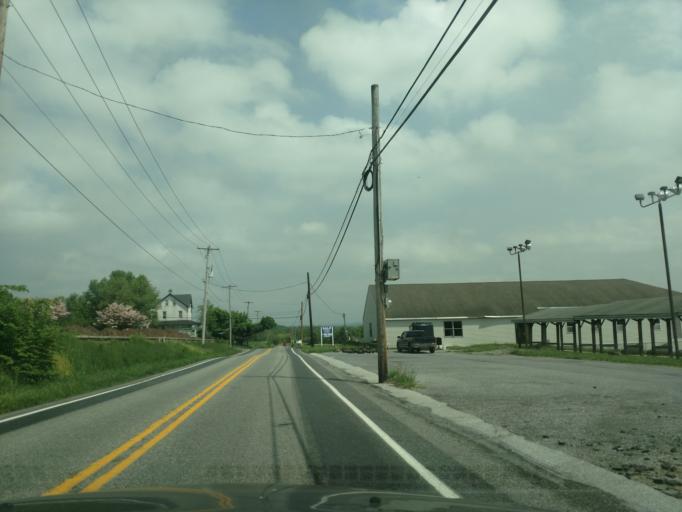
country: US
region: Pennsylvania
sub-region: Chester County
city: Spring City
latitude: 40.1551
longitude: -75.5685
